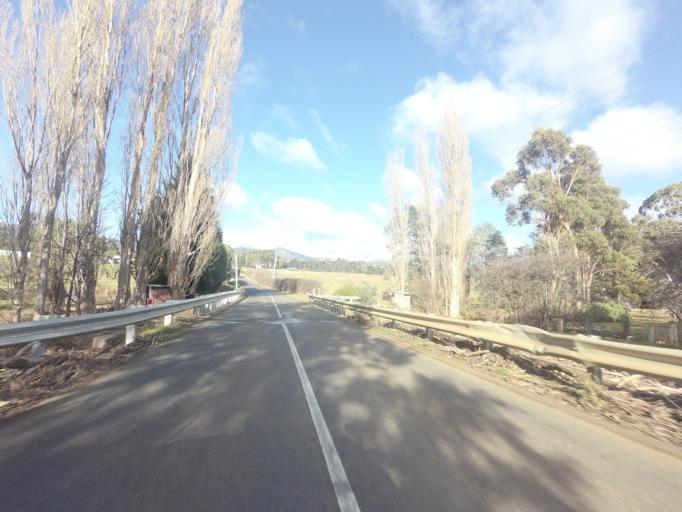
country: AU
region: Tasmania
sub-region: Derwent Valley
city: New Norfolk
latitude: -42.7928
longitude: 147.1221
